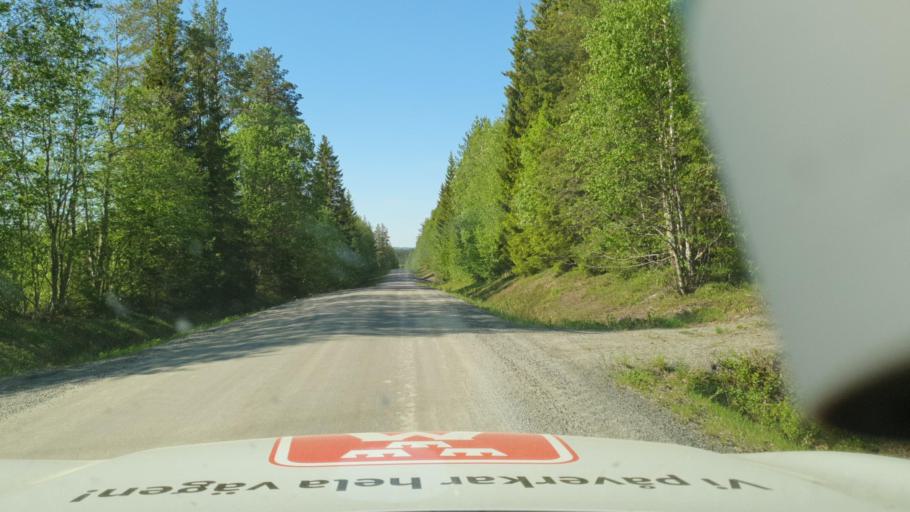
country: SE
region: Vaesterbotten
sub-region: Vannas Kommun
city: Vaennaes
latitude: 64.0134
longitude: 19.7413
